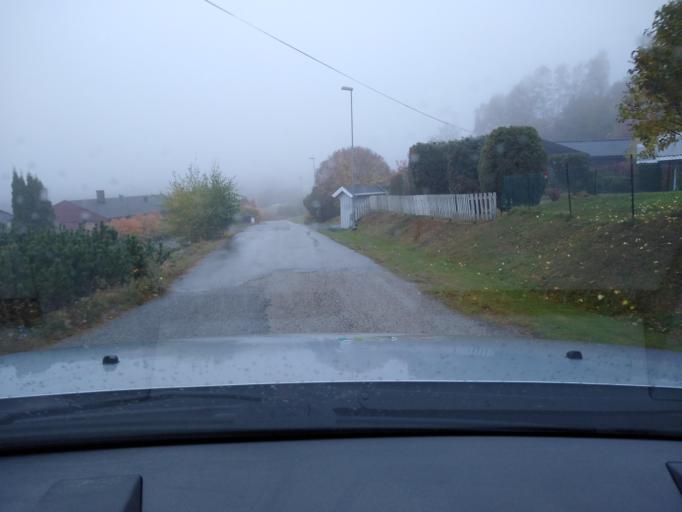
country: NO
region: Oppland
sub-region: Ringebu
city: Ringebu
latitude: 61.5316
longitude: 10.1518
